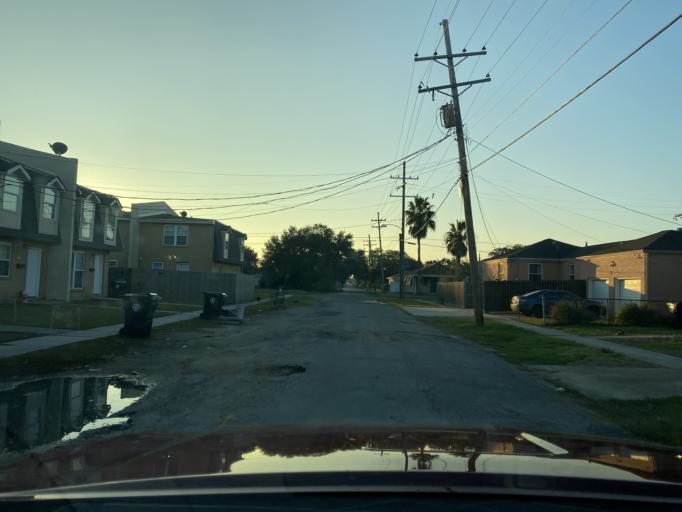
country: US
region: Louisiana
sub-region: Orleans Parish
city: New Orleans
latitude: 30.0235
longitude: -90.0547
